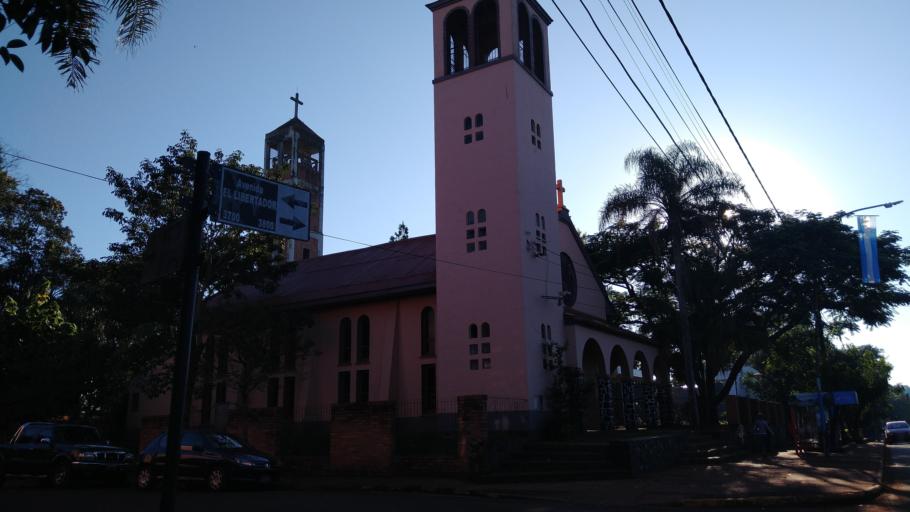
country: AR
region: Misiones
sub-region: Departamento de Montecarlo
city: Montecarlo
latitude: -26.5680
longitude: -54.7634
